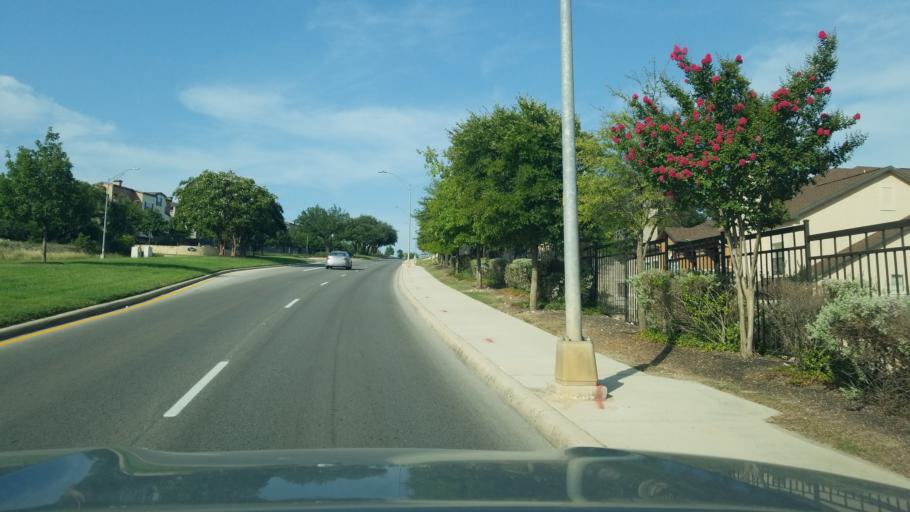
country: US
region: Texas
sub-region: Bexar County
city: Hollywood Park
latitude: 29.6485
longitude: -98.4643
